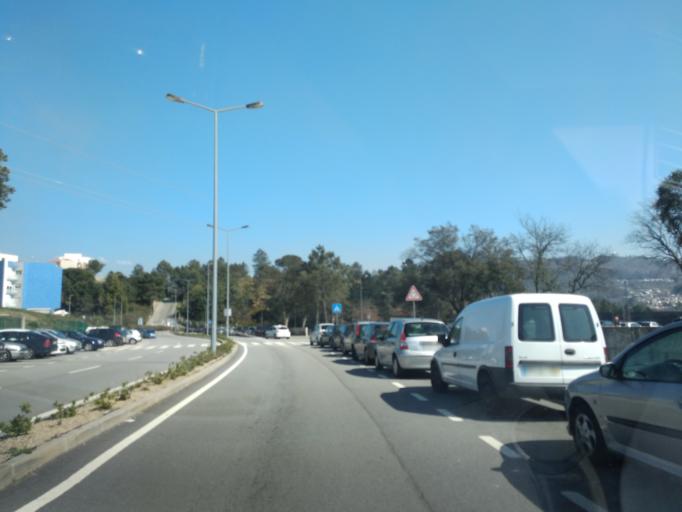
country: PT
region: Braga
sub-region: Braga
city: Adaufe
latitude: 41.5647
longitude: -8.4011
